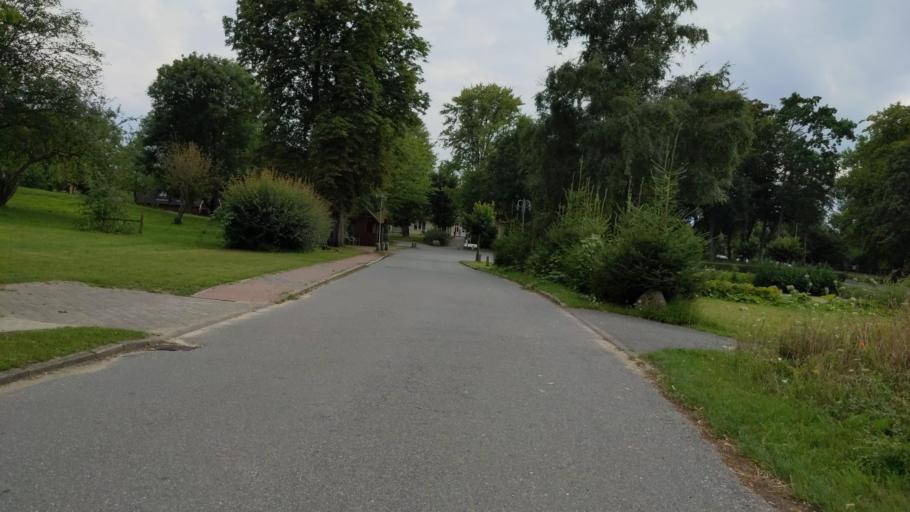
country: DE
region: Schleswig-Holstein
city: Altenkrempe
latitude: 54.1181
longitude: 10.8486
